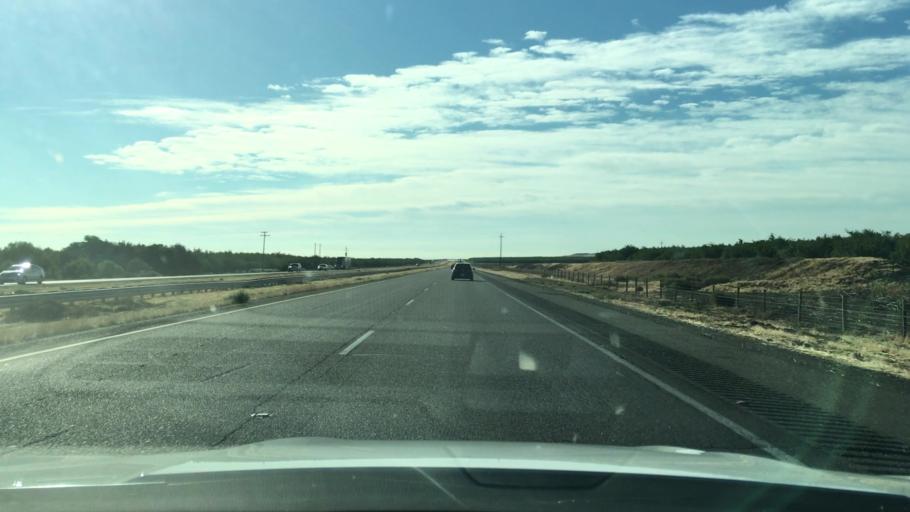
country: US
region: California
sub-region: Fresno County
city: Coalinga
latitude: 36.3950
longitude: -120.3579
